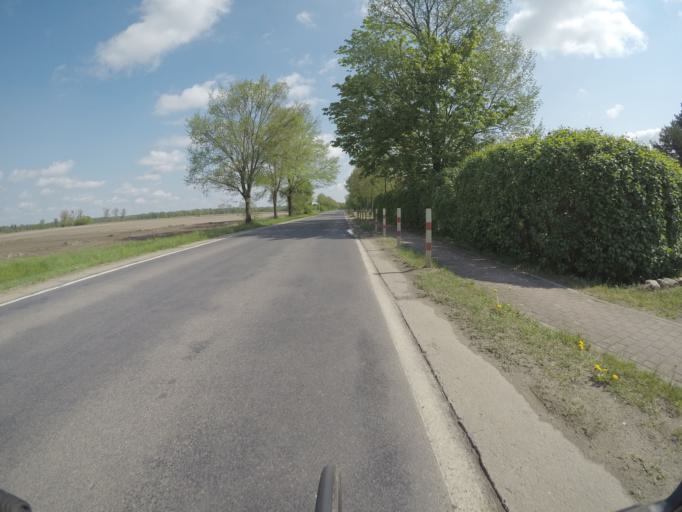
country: DE
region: Brandenburg
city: Marienwerder
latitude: 52.8283
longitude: 13.5625
